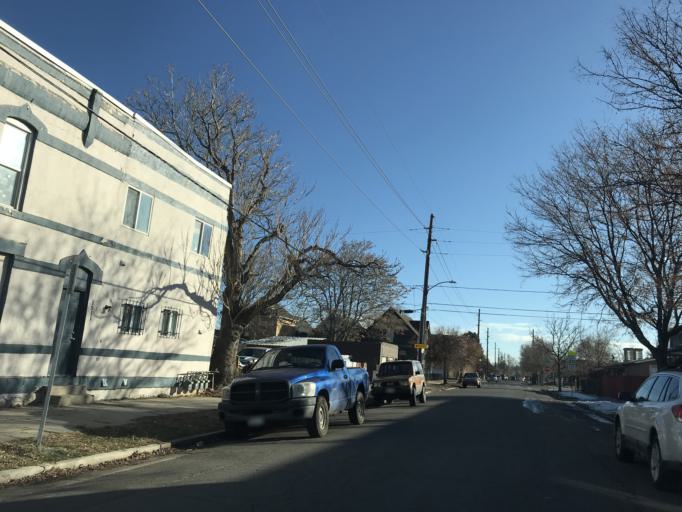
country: US
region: Colorado
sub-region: Denver County
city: Denver
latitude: 39.7683
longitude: -104.9695
